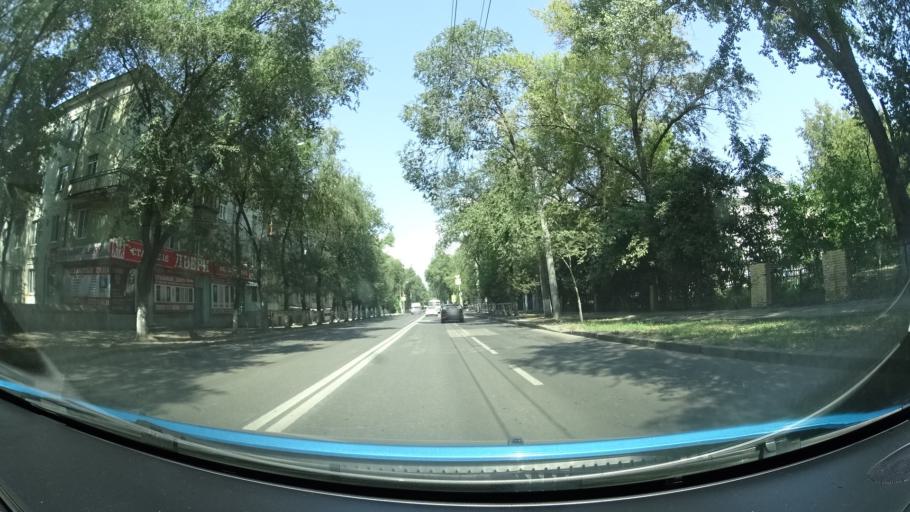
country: RU
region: Samara
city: Samara
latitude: 53.2063
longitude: 50.1617
